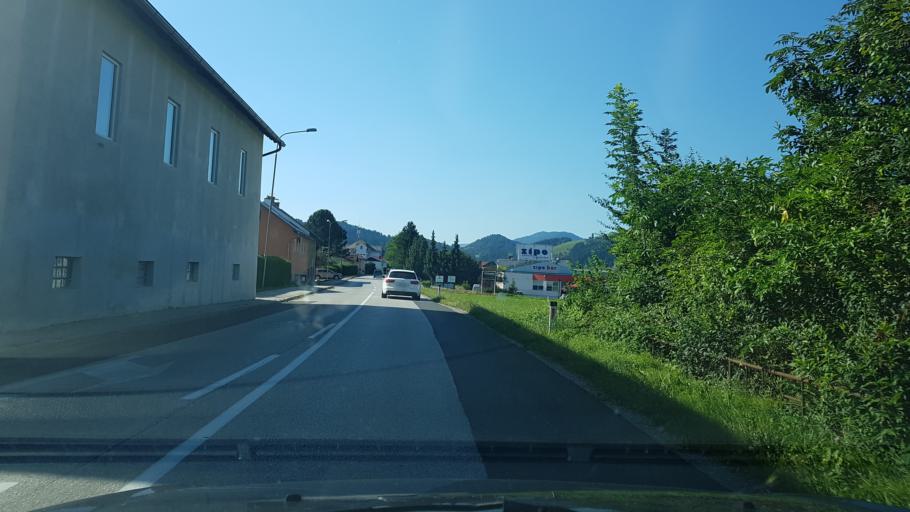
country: SI
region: Slovenj Gradec
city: Slovenj Gradec
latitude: 46.5008
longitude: 15.0912
